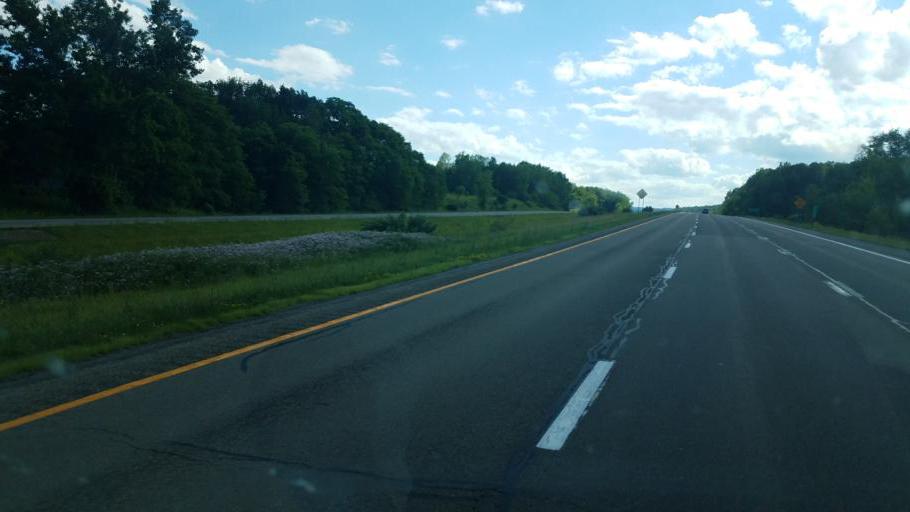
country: US
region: New York
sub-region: Steuben County
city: Hornell
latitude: 42.3637
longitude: -77.7004
